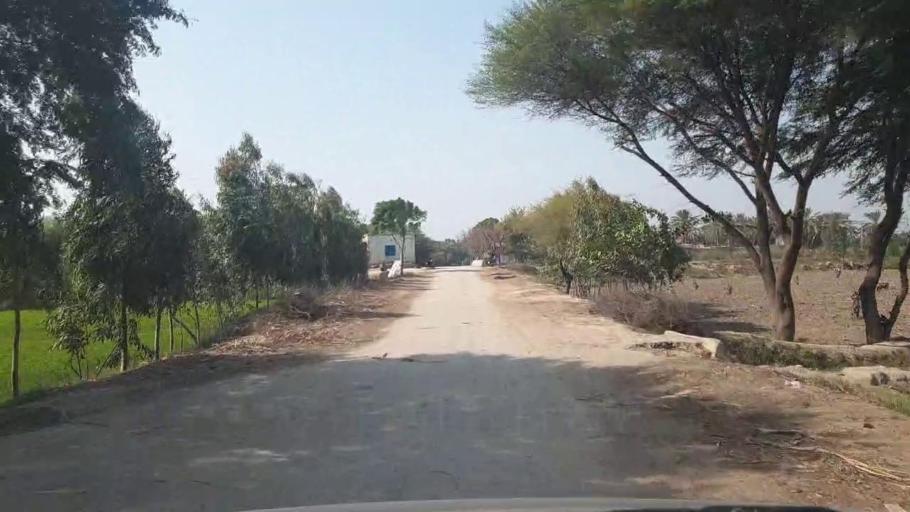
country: PK
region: Sindh
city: Tando Adam
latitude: 25.7694
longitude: 68.6054
